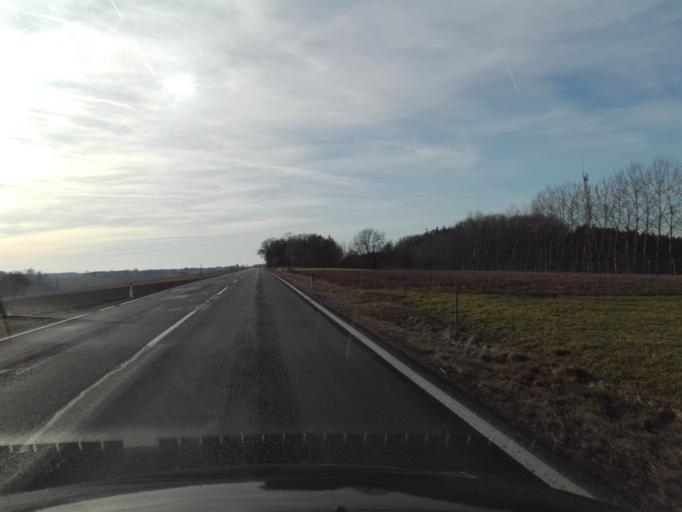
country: AT
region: Lower Austria
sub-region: Politischer Bezirk Amstetten
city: Zeillern
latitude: 48.1193
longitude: 14.7925
